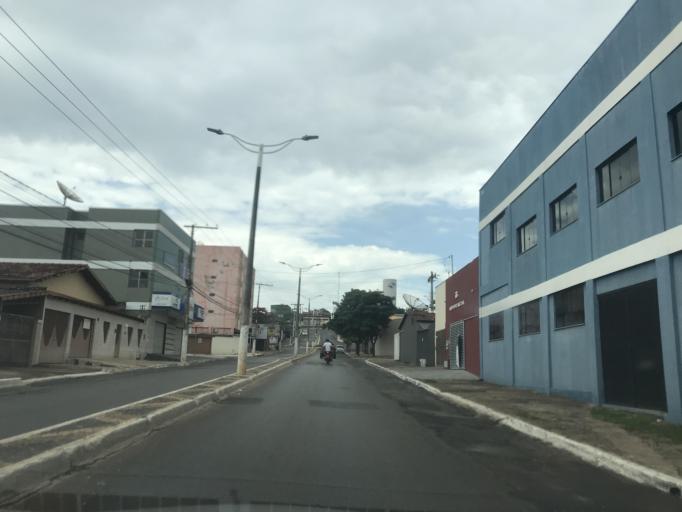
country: BR
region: Goias
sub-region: Luziania
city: Luziania
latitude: -16.2547
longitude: -47.9590
